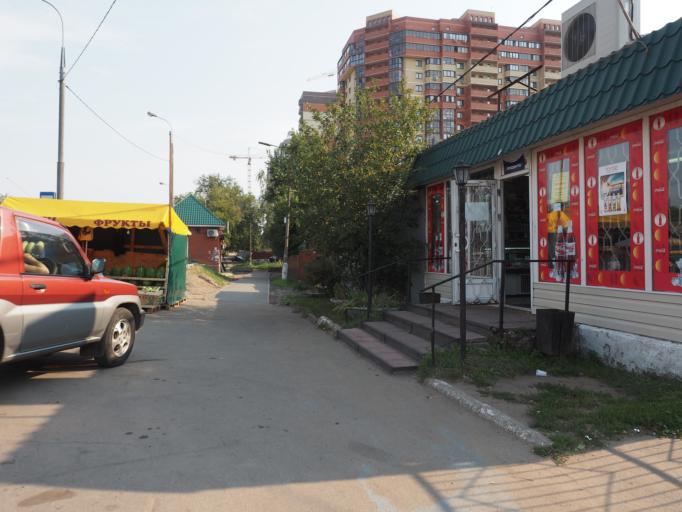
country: RU
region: Moskovskaya
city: Oktyabr'skiy
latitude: 55.6110
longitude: 37.9752
